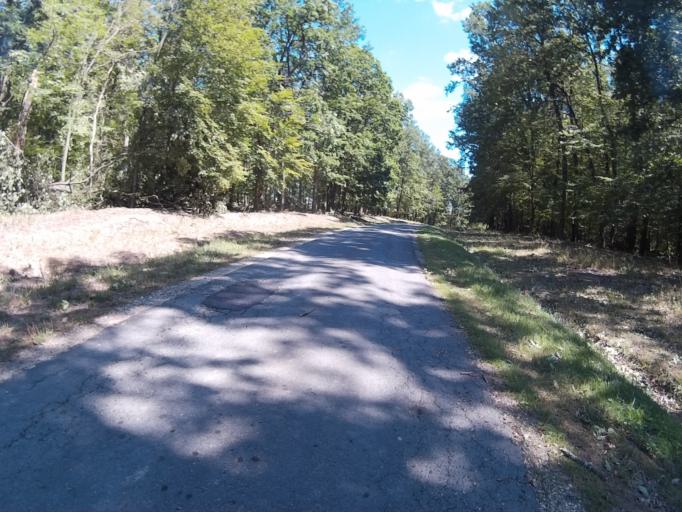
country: HU
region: Zala
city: Zalalovo
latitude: 46.7929
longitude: 16.6162
